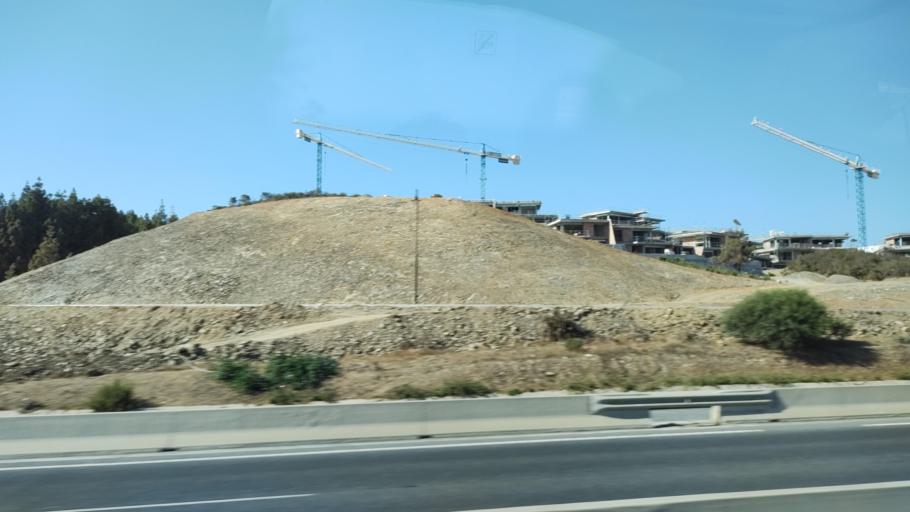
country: ES
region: Andalusia
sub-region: Provincia de Malaga
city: Fuengirola
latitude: 36.5070
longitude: -4.6588
